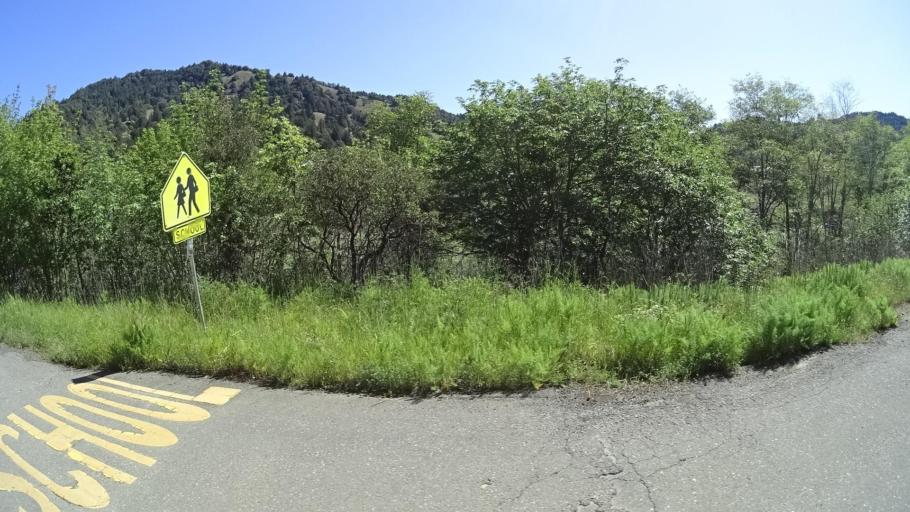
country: US
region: California
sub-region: Humboldt County
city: Rio Dell
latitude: 40.2413
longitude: -124.1225
